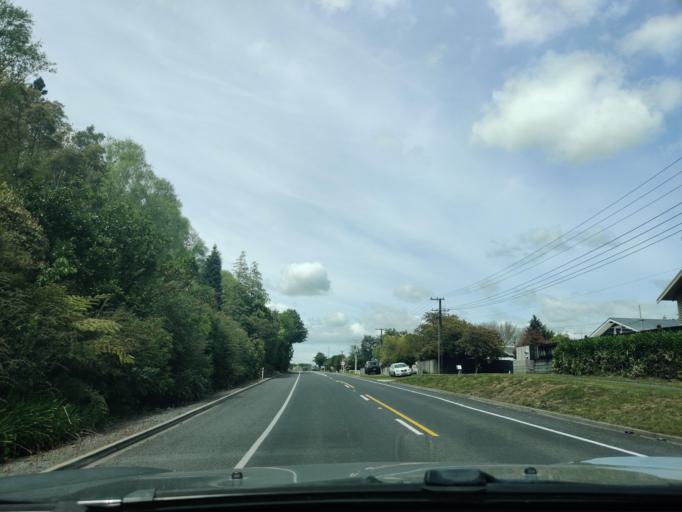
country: NZ
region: Taranaki
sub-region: New Plymouth District
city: New Plymouth
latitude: -39.1613
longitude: 174.2086
